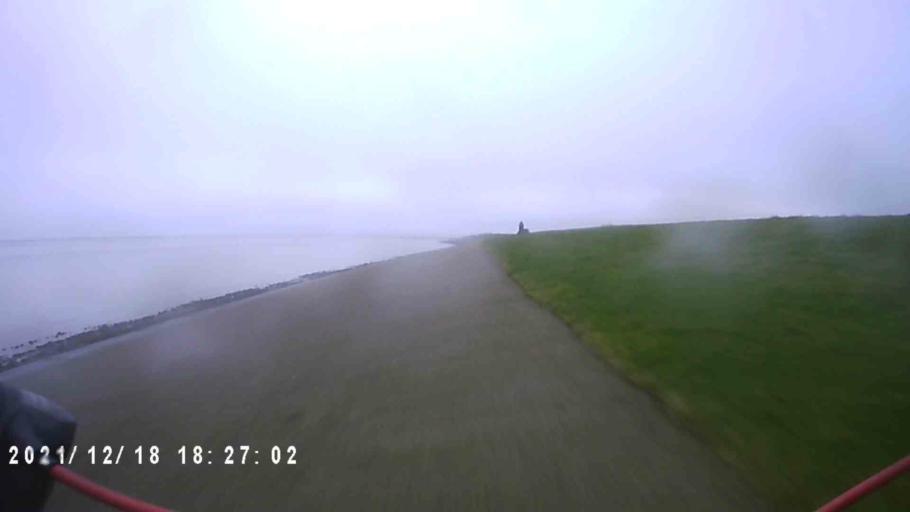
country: NL
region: Friesland
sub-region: Gemeente Dongeradeel
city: Ternaard
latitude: 53.4007
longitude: 6.0061
